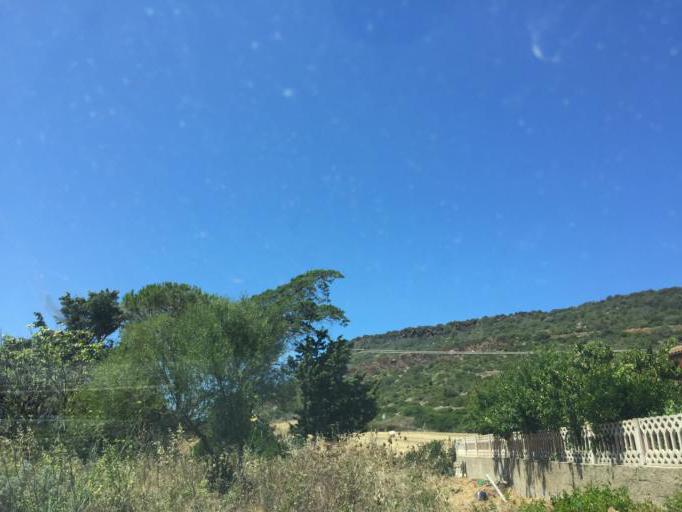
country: IT
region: Sardinia
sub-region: Provincia di Sassari
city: Castelsardo
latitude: 40.8939
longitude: 8.7442
